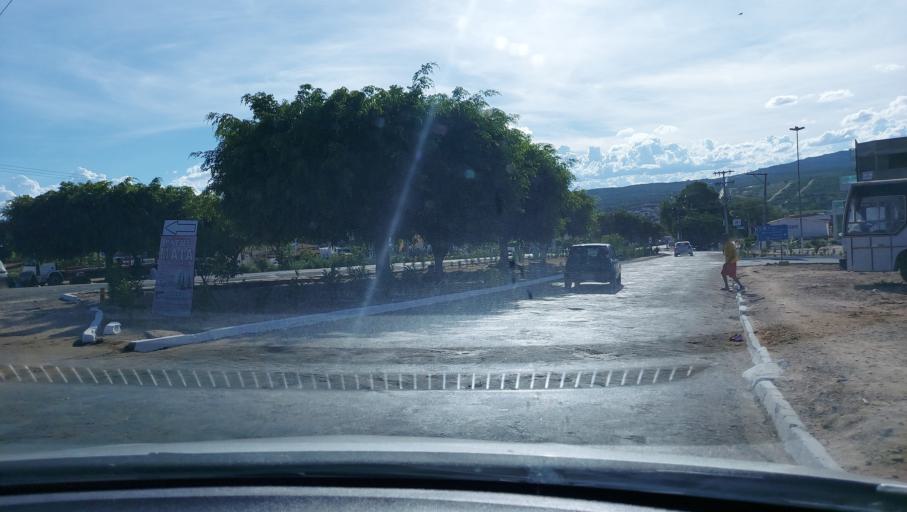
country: BR
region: Bahia
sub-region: Seabra
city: Seabra
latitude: -12.4272
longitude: -41.7695
